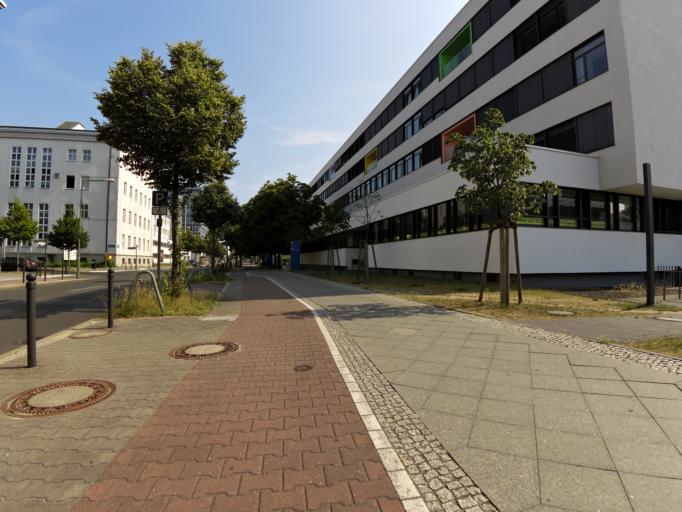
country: DE
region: Berlin
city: Adlershof
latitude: 52.4317
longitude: 13.5383
